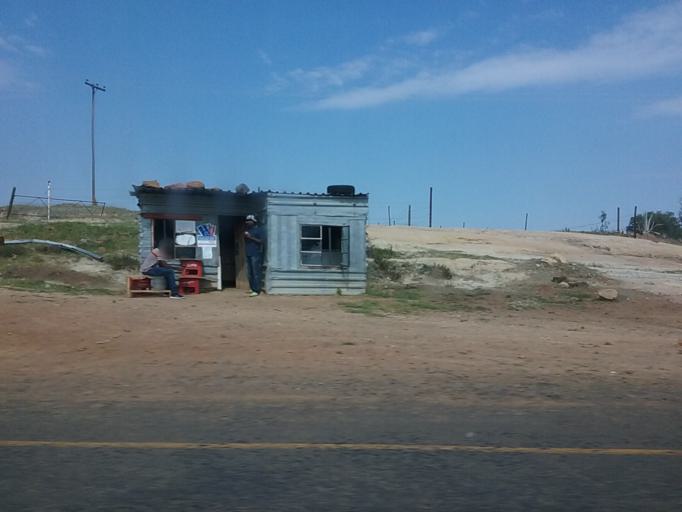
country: LS
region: Berea
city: Teyateyaneng
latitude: -29.1262
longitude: 27.9821
